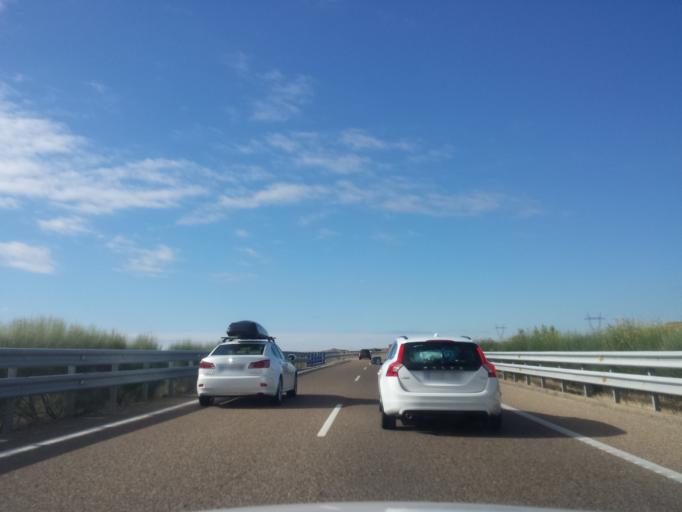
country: ES
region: Castille and Leon
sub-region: Provincia de Leon
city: Algadefe
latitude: 42.2373
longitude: -5.5918
